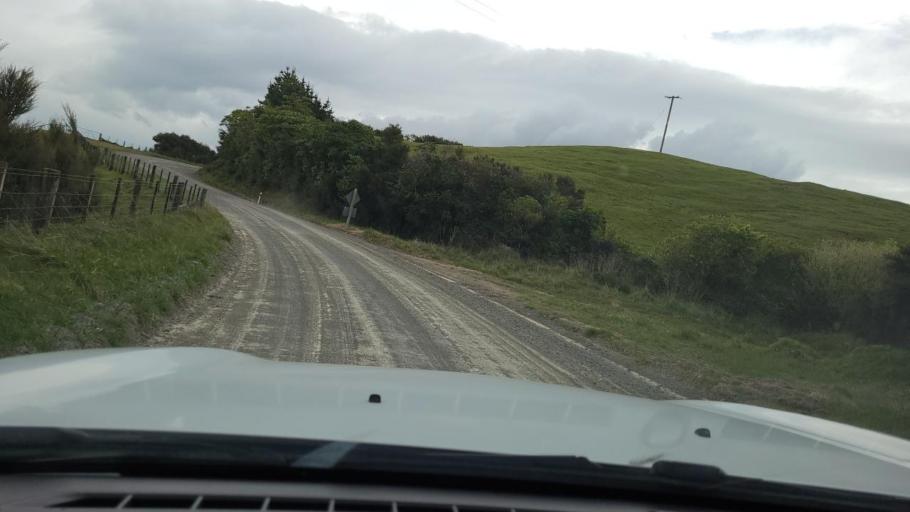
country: NZ
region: Hawke's Bay
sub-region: Napier City
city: Napier
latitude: -39.3107
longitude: 176.8326
